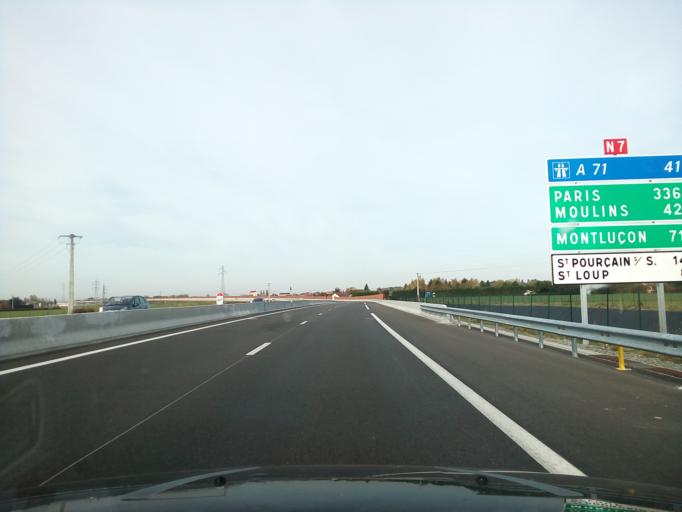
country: FR
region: Auvergne
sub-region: Departement de l'Allier
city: Varennes-sur-Allier
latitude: 46.3028
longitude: 3.4177
